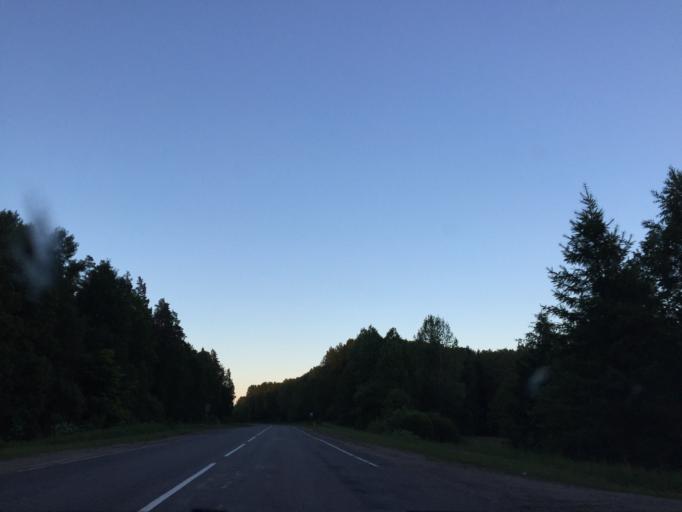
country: LV
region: Smiltene
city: Smiltene
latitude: 57.4359
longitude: 26.1709
